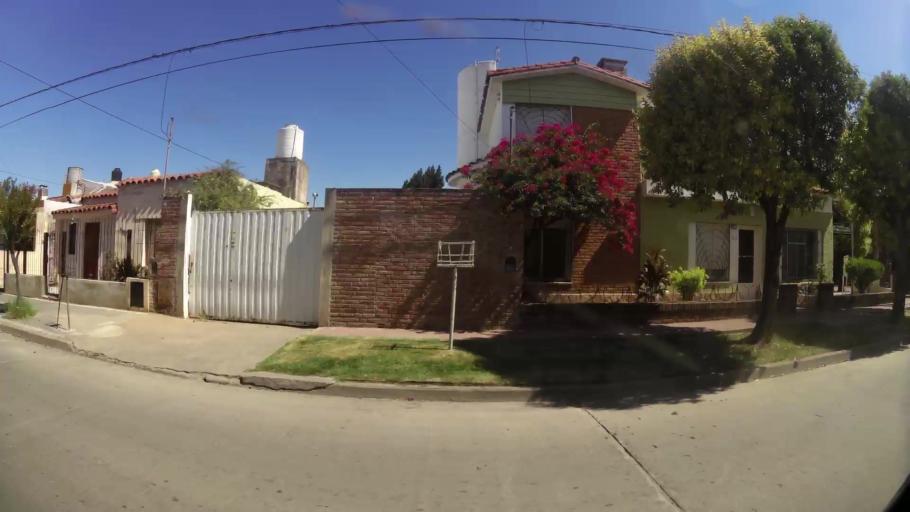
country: AR
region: Cordoba
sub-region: Departamento de Capital
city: Cordoba
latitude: -31.3756
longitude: -64.1381
